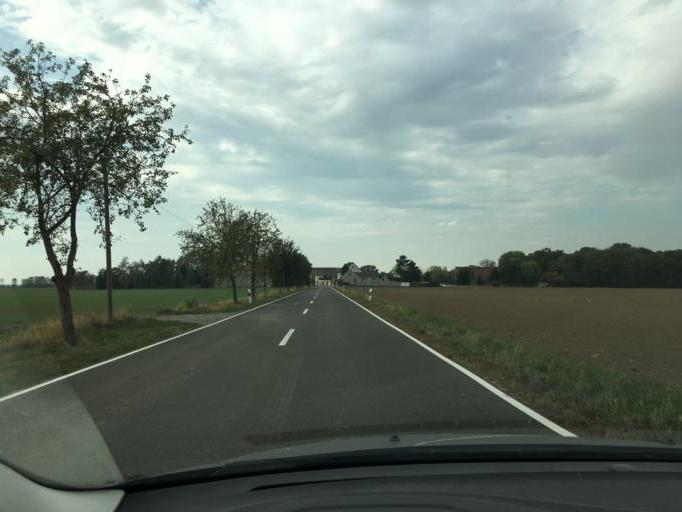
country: DE
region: Saxony
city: Zwochau
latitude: 51.4998
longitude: 12.2471
